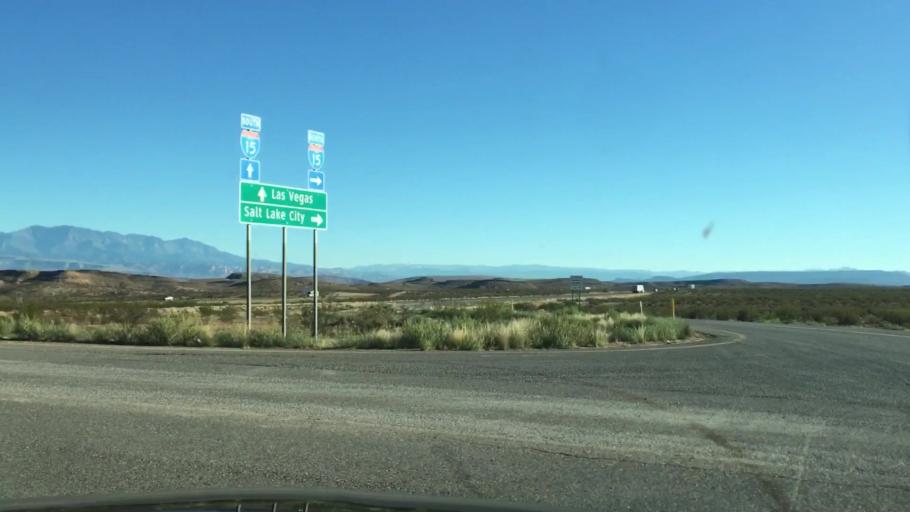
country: US
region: Utah
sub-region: Washington County
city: Saint George
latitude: 36.9808
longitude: -113.6449
